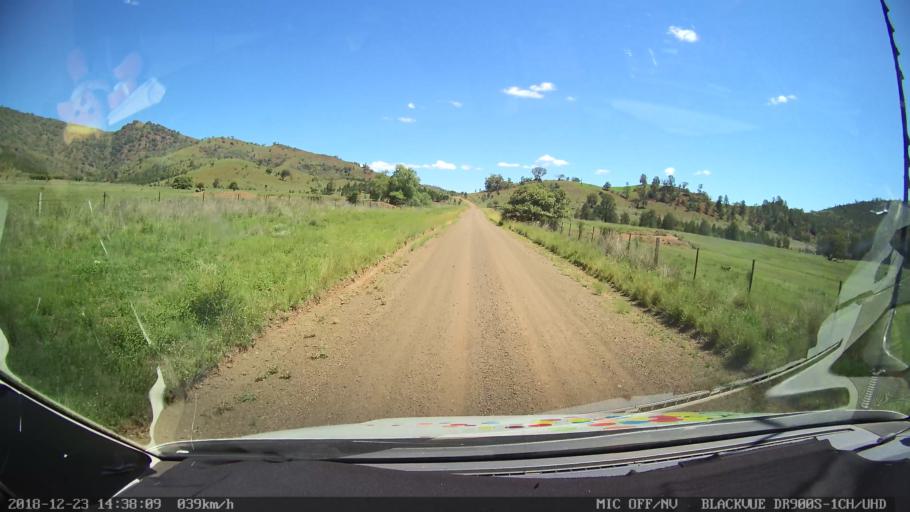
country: AU
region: New South Wales
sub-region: Tamworth Municipality
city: Manilla
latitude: -30.6199
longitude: 150.9061
